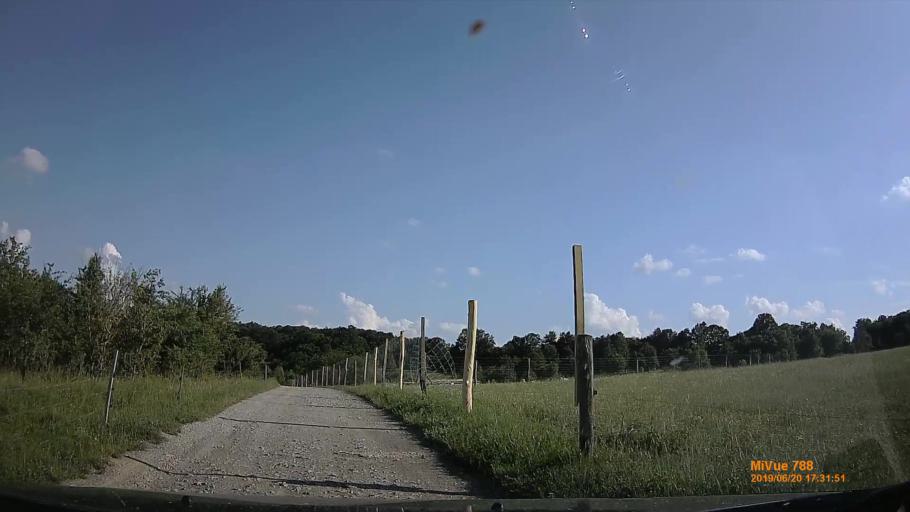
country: HU
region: Baranya
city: Buekkoesd
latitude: 46.1511
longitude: 18.0096
